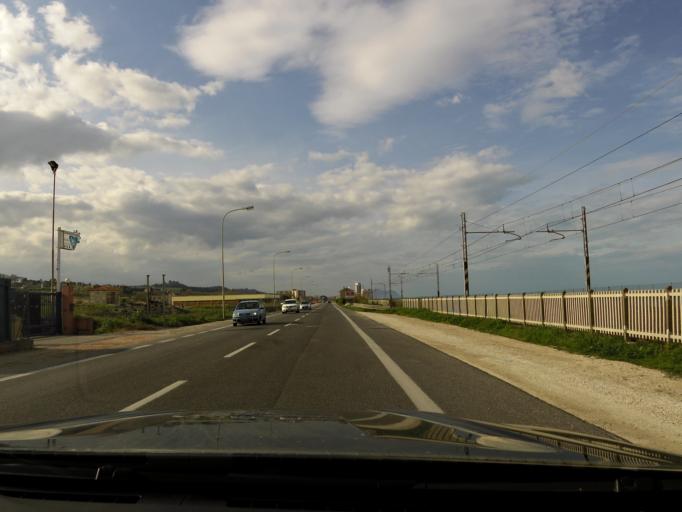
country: IT
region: The Marches
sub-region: Provincia di Macerata
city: Porto Potenza Picena
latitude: 43.3388
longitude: 13.7081
